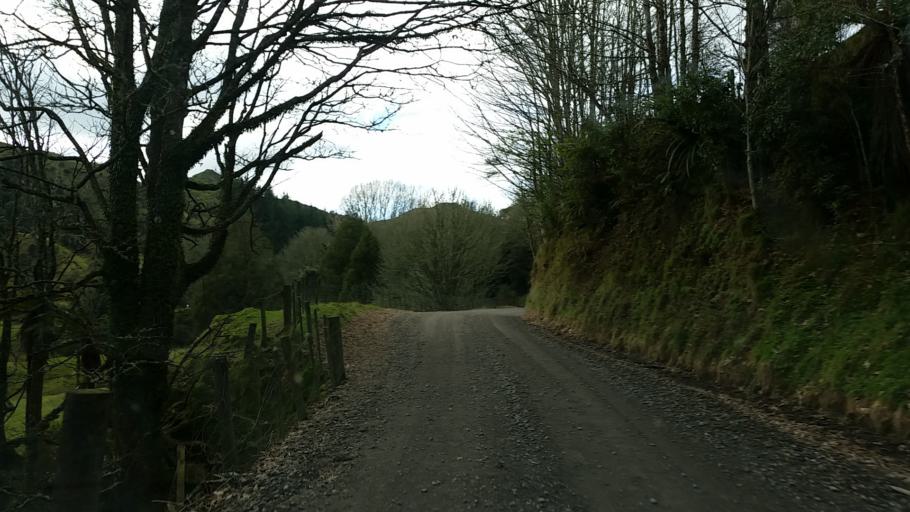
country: NZ
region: Taranaki
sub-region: New Plymouth District
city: Waitara
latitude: -39.1633
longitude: 174.5735
